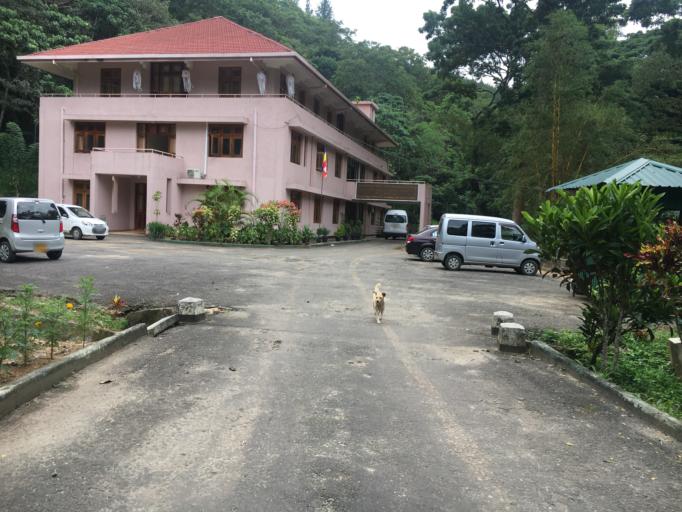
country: LK
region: Central
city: Kandy
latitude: 7.2561
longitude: 80.5998
